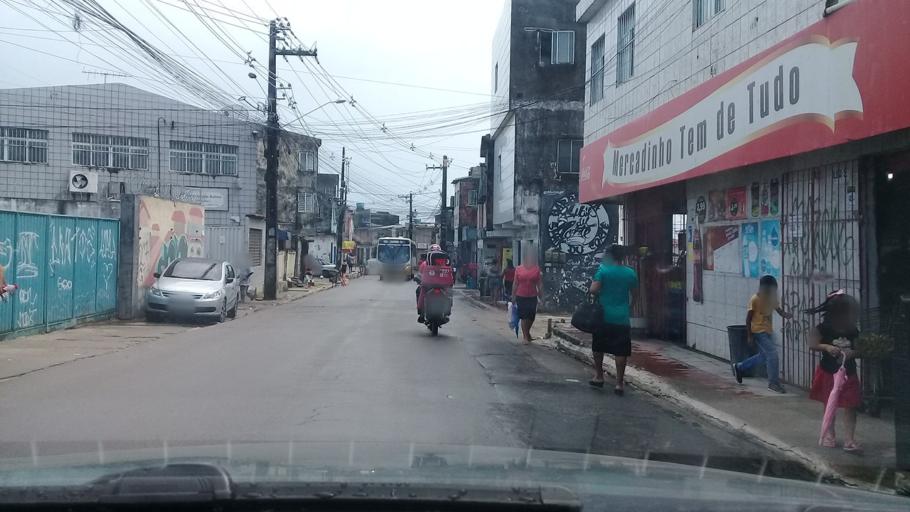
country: BR
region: Pernambuco
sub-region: Jaboatao Dos Guararapes
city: Jaboatao dos Guararapes
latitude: -8.1129
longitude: -34.9560
